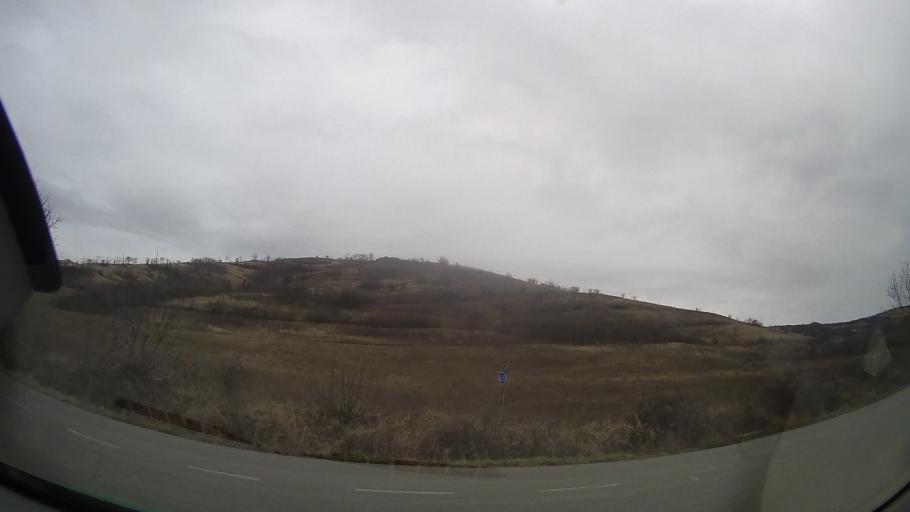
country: RO
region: Mures
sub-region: Comuna Bala
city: Bala
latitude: 46.7167
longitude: 24.5538
